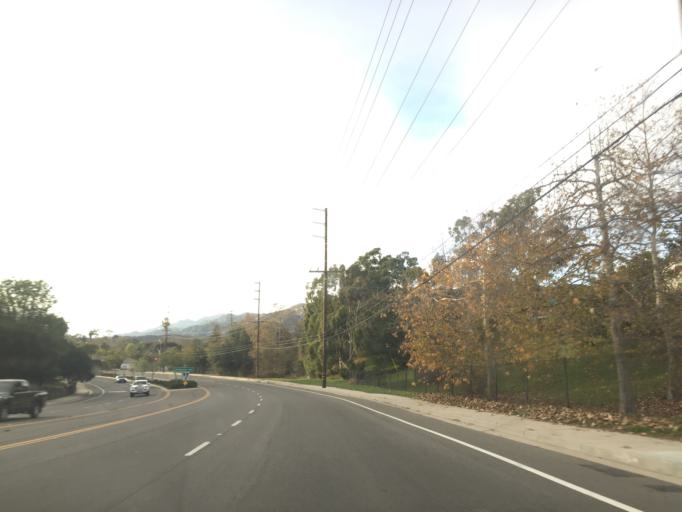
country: US
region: California
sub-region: Santa Barbara County
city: Goleta
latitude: 34.4526
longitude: -119.8058
